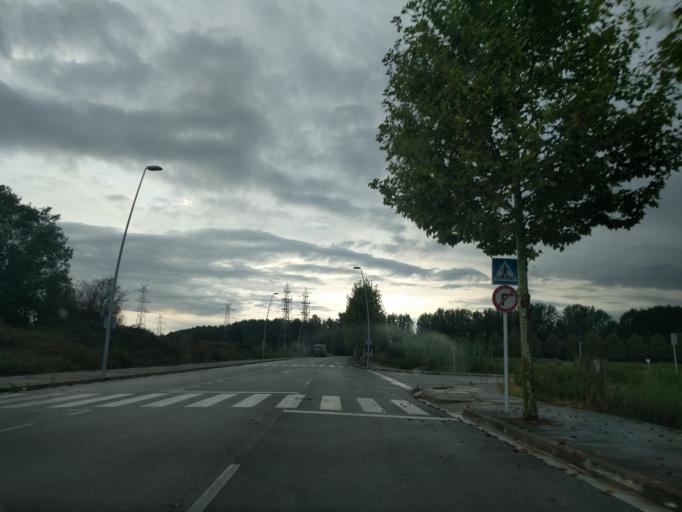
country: ES
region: Catalonia
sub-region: Provincia de Girona
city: Fornells de la Selva
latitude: 41.9446
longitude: 2.7969
